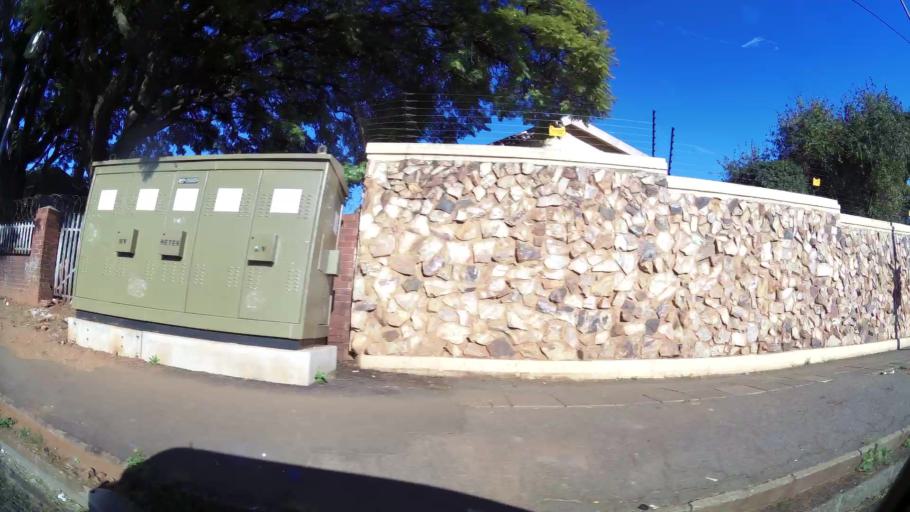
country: ZA
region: Gauteng
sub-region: City of Johannesburg Metropolitan Municipality
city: Johannesburg
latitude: -26.1966
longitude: 28.1124
